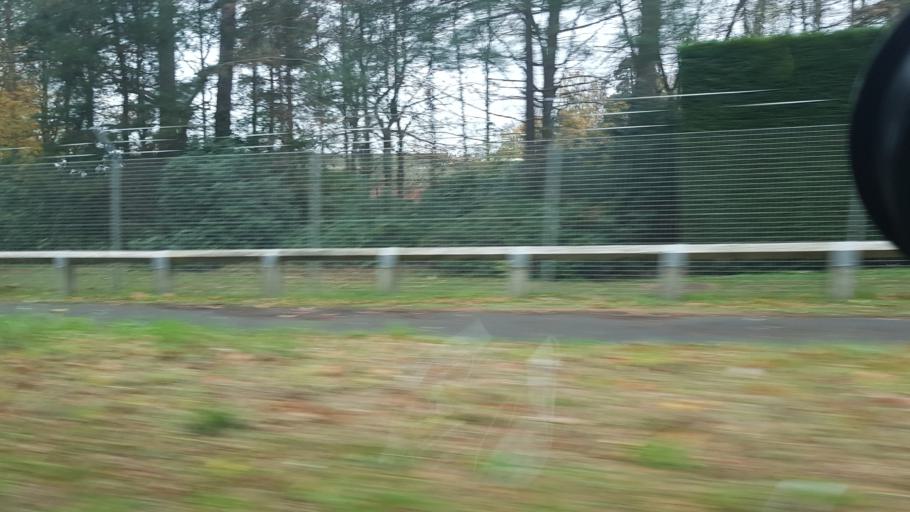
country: GB
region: England
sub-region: Hampshire
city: Yateley
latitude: 51.3168
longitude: -0.8192
